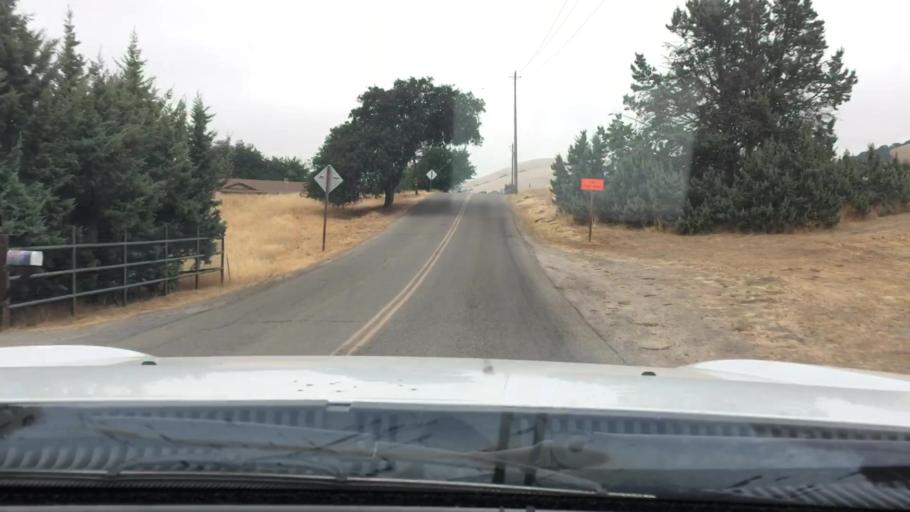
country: US
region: California
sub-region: San Luis Obispo County
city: Atascadero
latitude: 35.5090
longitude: -120.6404
